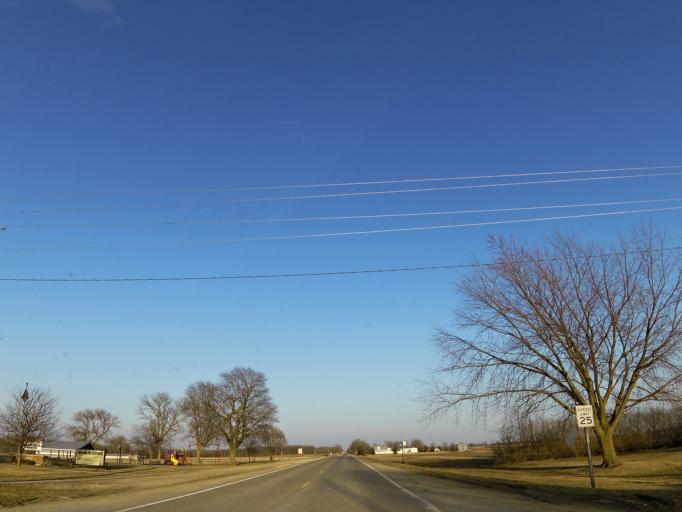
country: US
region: Iowa
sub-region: Mitchell County
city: Saint Ansgar
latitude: 43.4150
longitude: -93.0150
